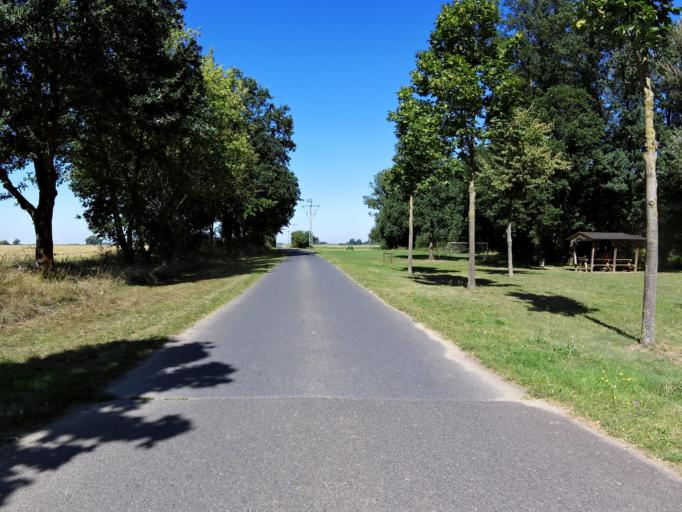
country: DE
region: Saxony-Anhalt
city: Pretzsch
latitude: 51.7441
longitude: 12.8361
